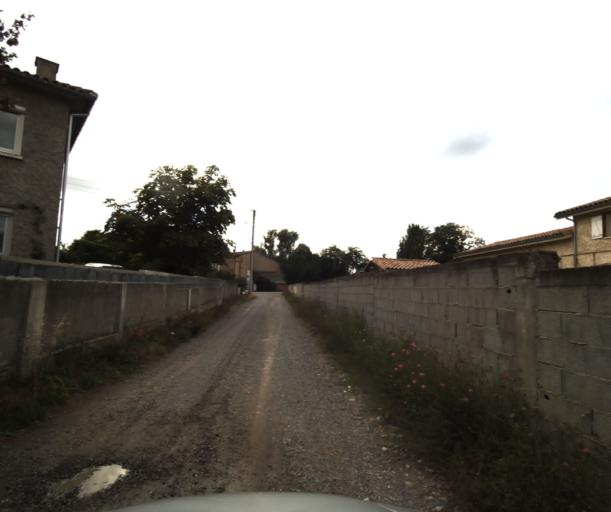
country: FR
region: Midi-Pyrenees
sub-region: Departement de la Haute-Garonne
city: Eaunes
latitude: 43.4312
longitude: 1.3468
